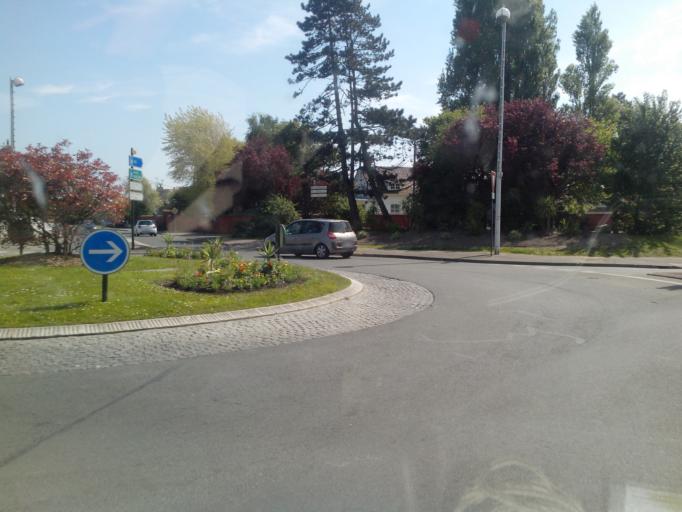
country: FR
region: Nord-Pas-de-Calais
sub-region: Departement du Pas-de-Calais
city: Berck
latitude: 50.4113
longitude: 1.5937
